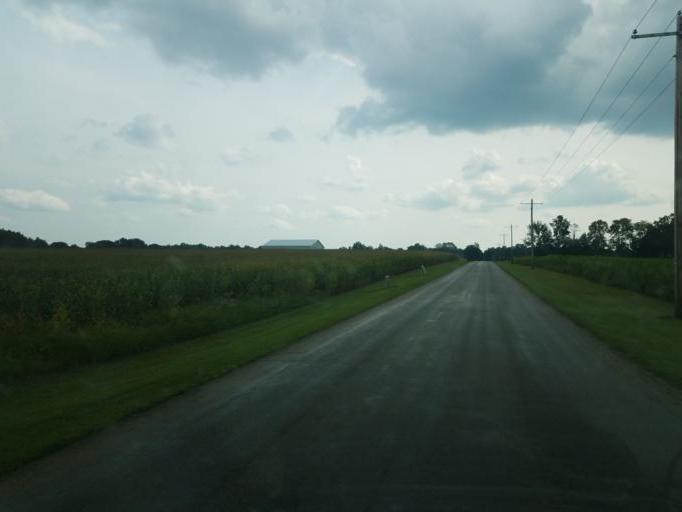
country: US
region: Ohio
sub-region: Knox County
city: Gambier
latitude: 40.3678
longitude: -82.3539
